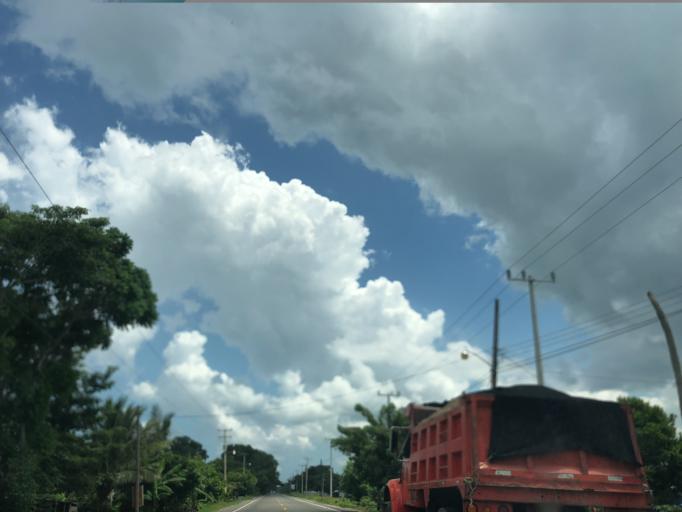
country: MX
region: Tabasco
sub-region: Comalcalco
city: Oriente 6ta. Seccion (Los Mulatos)
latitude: 18.1748
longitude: -93.2364
